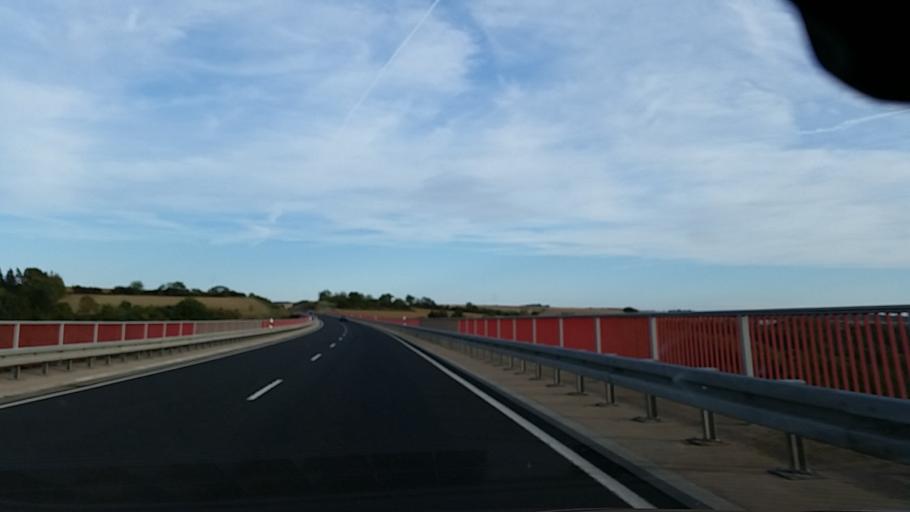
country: DE
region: Bavaria
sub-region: Regierungsbezirk Unterfranken
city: Mellrichstadt
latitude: 50.4430
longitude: 10.3136
